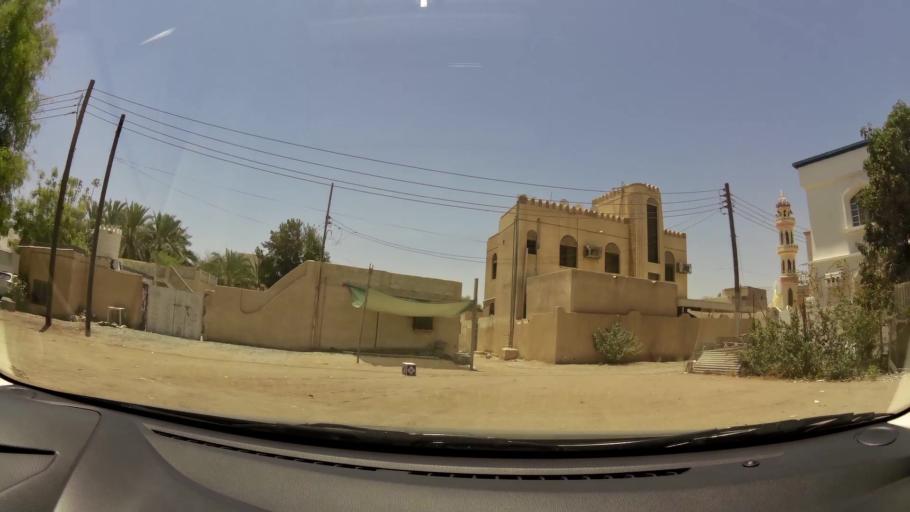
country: OM
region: Muhafazat Masqat
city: As Sib al Jadidah
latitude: 23.6323
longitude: 58.2454
